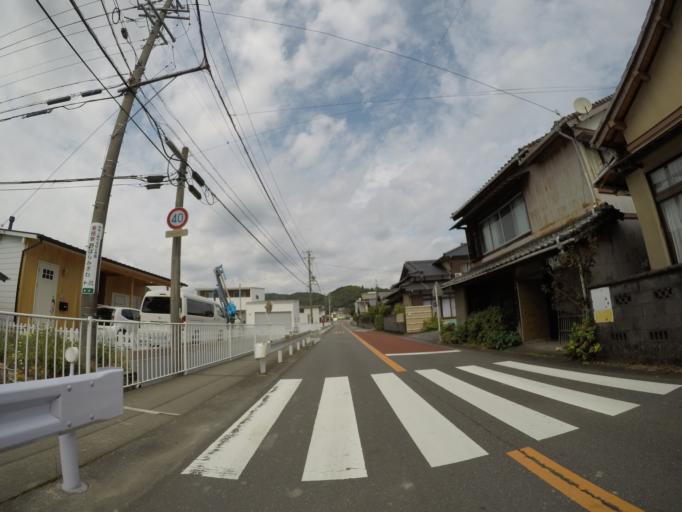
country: JP
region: Shizuoka
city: Shimada
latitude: 34.8573
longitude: 138.1803
